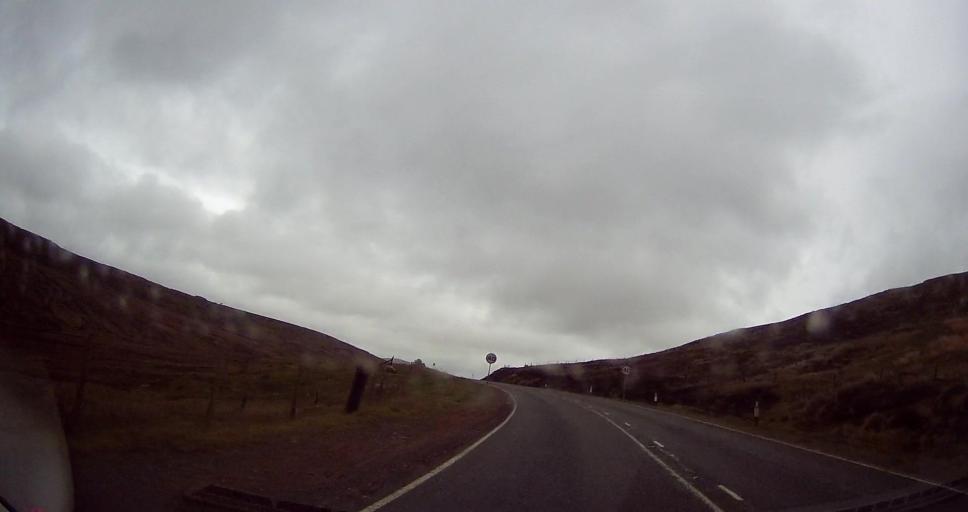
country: GB
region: Scotland
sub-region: Shetland Islands
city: Lerwick
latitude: 60.3203
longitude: -1.2490
